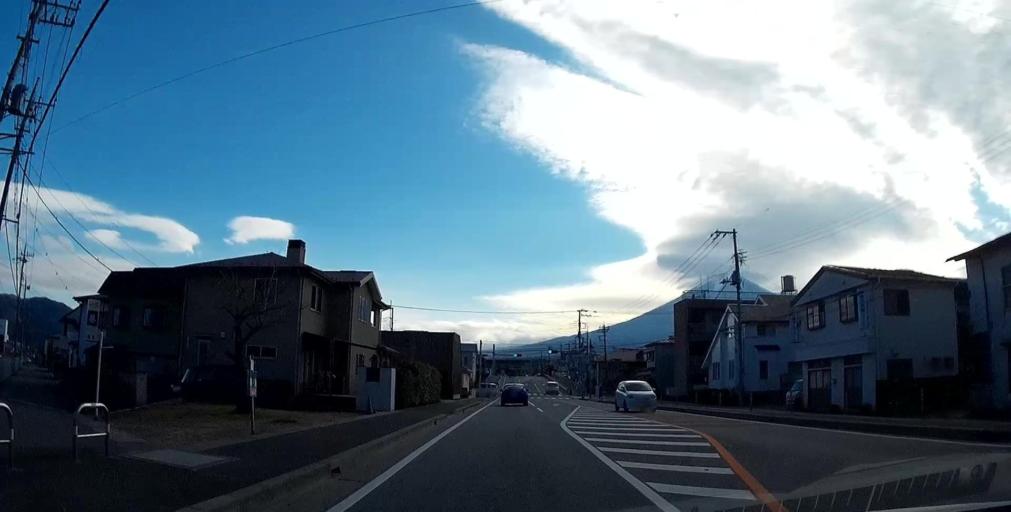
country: JP
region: Yamanashi
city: Fujikawaguchiko
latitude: 35.4928
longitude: 138.7934
